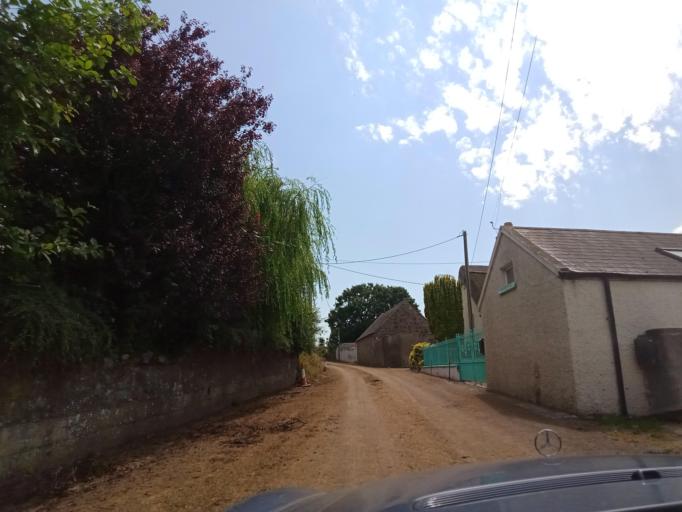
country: IE
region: Leinster
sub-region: Kilkenny
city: Mooncoin
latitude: 52.2694
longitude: -7.2277
